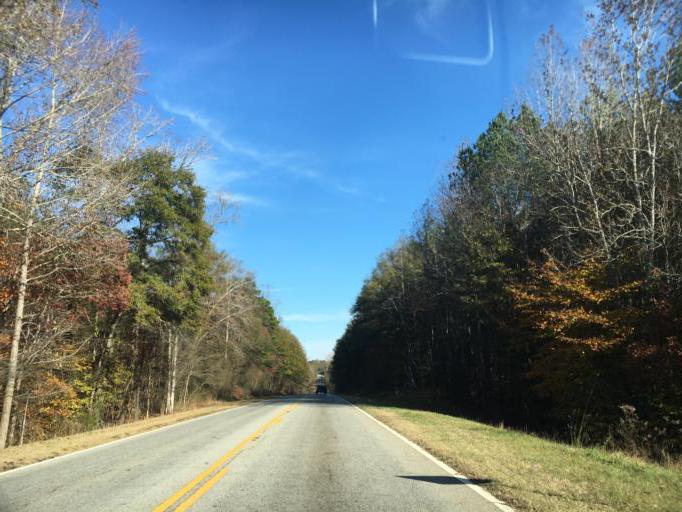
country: US
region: South Carolina
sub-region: Spartanburg County
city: Wellford
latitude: 34.9665
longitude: -82.1080
